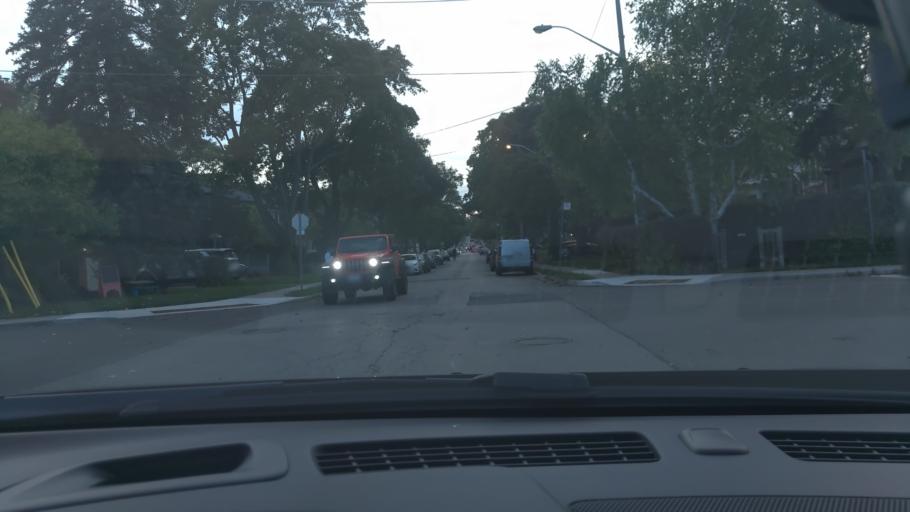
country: CA
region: Ontario
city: Toronto
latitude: 43.7180
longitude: -79.3691
